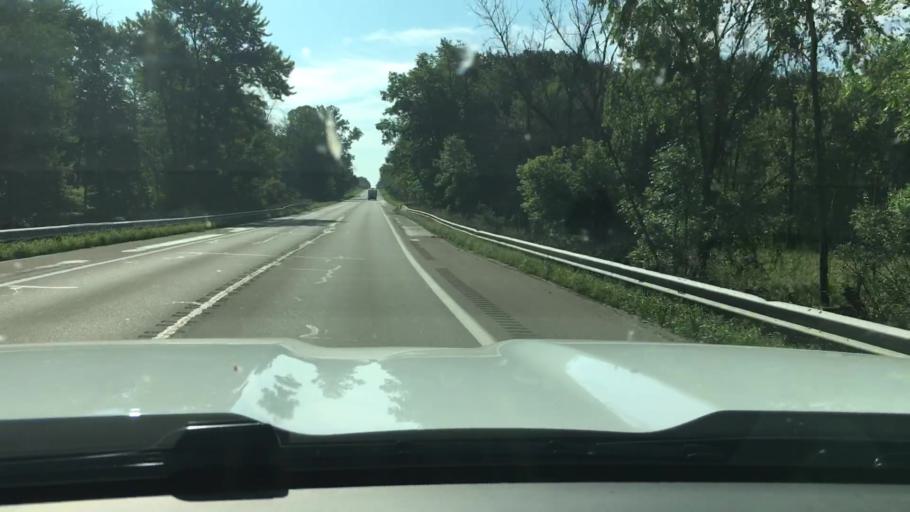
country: US
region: Michigan
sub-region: Montcalm County
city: Edmore
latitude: 43.4251
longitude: -85.1453
